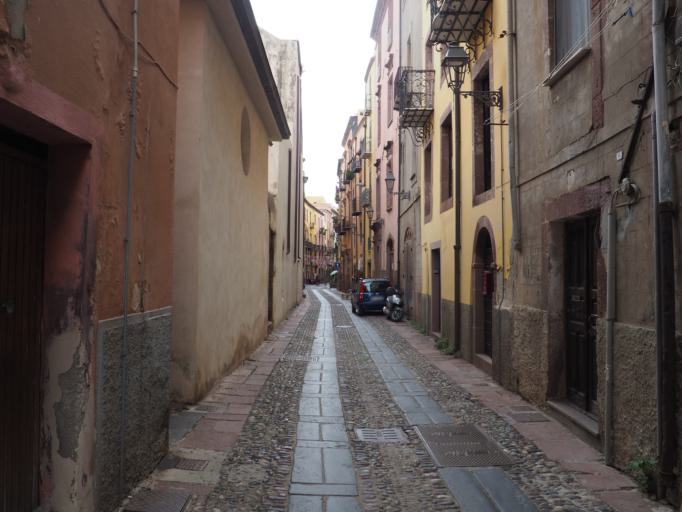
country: IT
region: Sardinia
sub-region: Provincia di Oristano
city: Bosa
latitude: 40.2952
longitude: 8.5054
